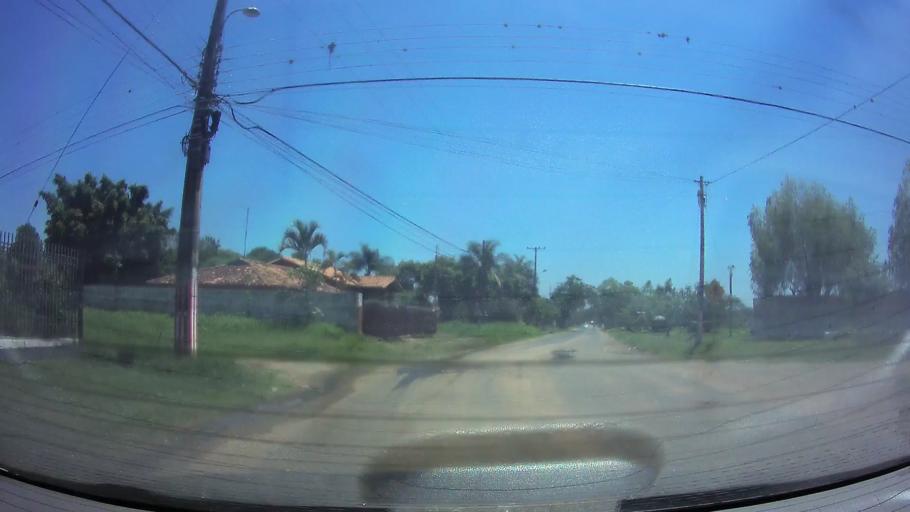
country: PY
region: Central
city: San Lorenzo
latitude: -25.3266
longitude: -57.4849
